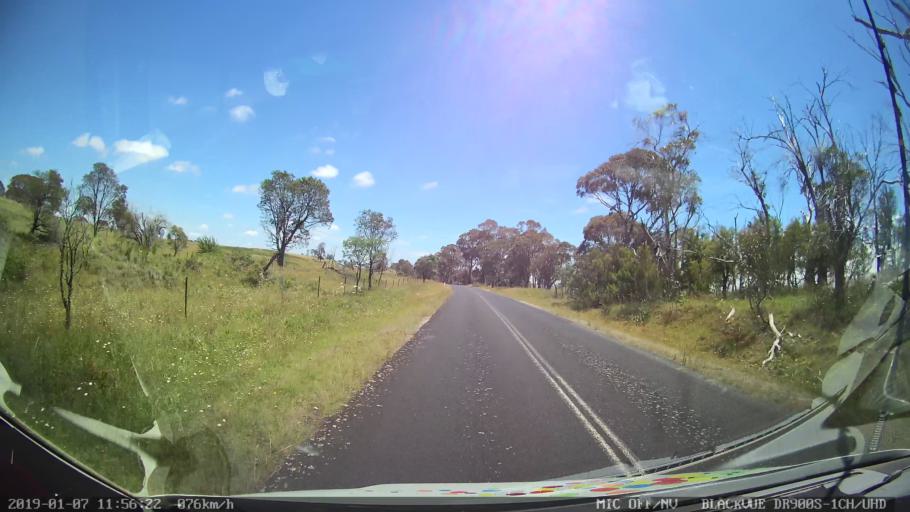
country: AU
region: New South Wales
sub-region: Guyra
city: Guyra
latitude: -30.2754
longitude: 151.6739
